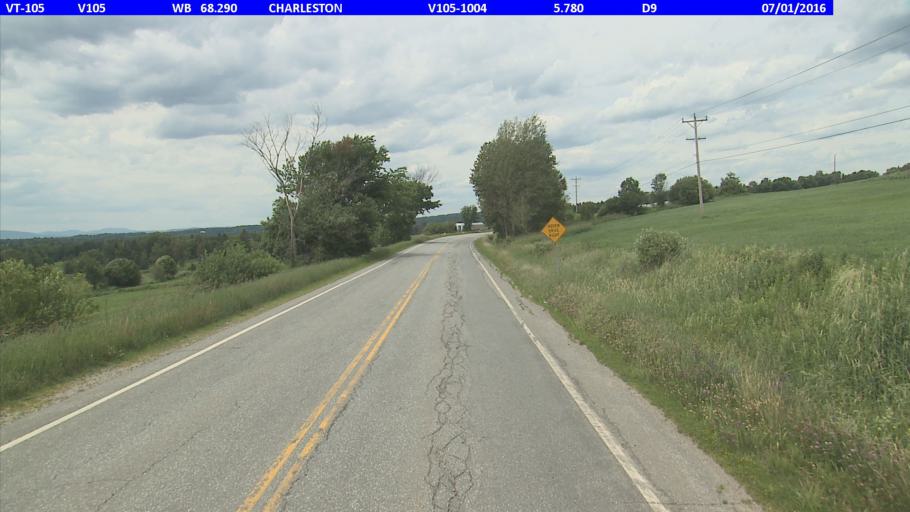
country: US
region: Vermont
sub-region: Orleans County
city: Newport
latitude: 44.8443
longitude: -72.0140
